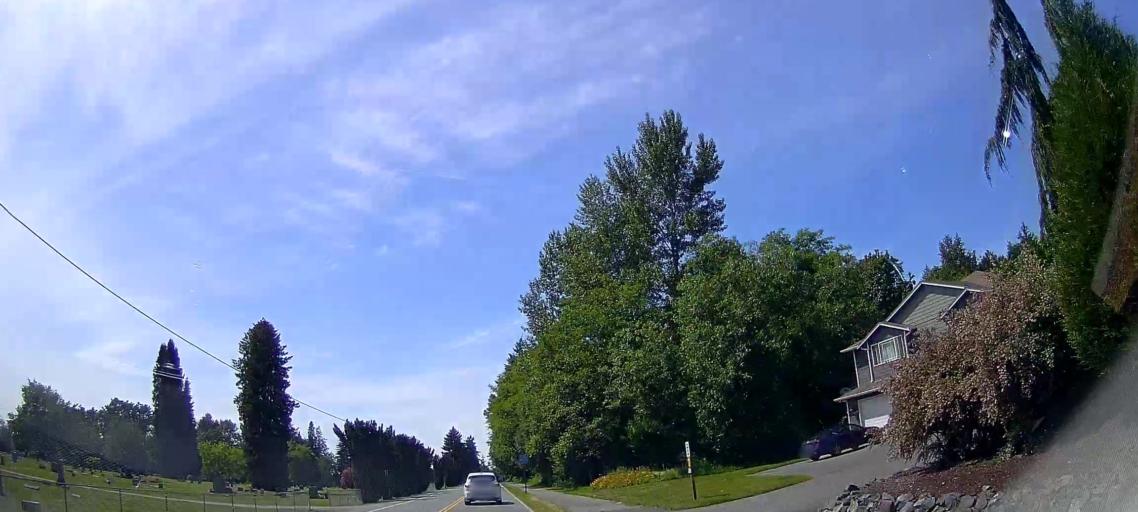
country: US
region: Washington
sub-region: Snohomish County
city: Stanwood
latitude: 48.2328
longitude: -122.3327
